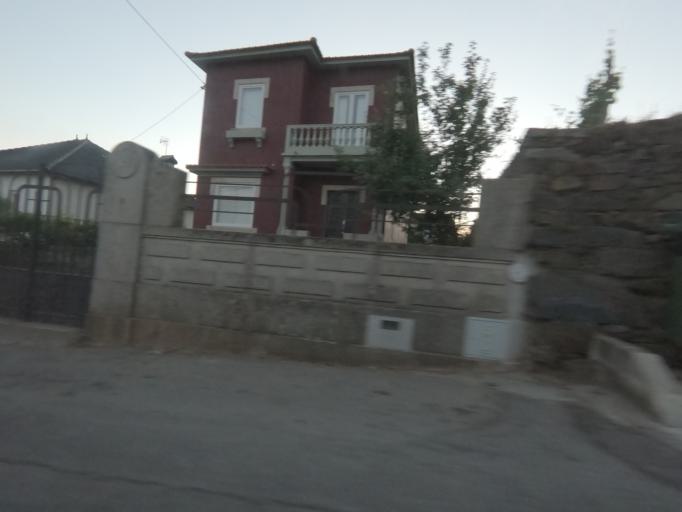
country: PT
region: Vila Real
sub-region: Peso da Regua
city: Peso da Regua
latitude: 41.1799
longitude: -7.7240
